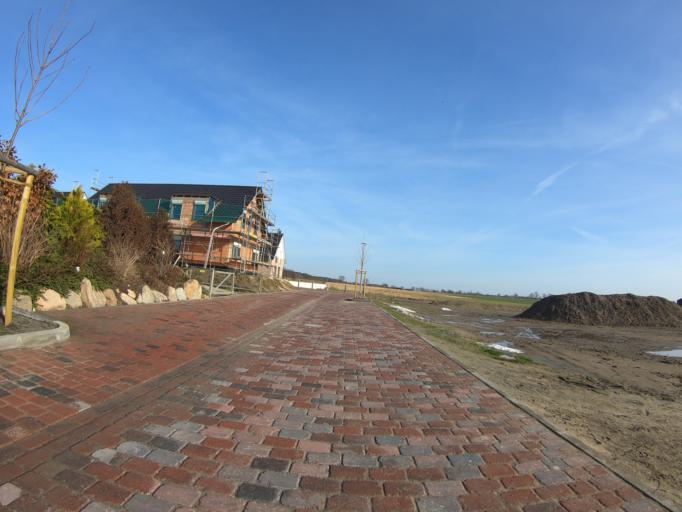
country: DE
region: Lower Saxony
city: Rotgesbuttel
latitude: 52.4177
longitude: 10.5381
